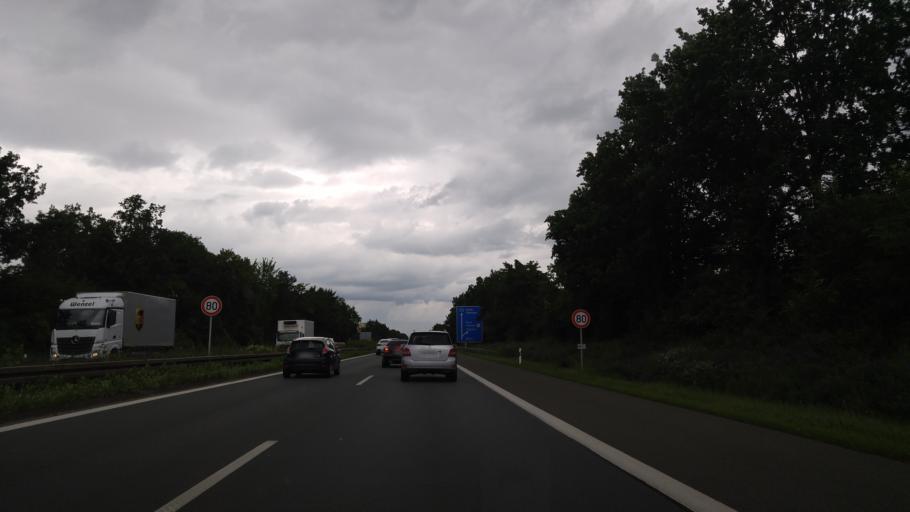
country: DE
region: Bavaria
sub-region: Regierungsbezirk Mittelfranken
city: Furth
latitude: 49.4864
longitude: 11.0033
